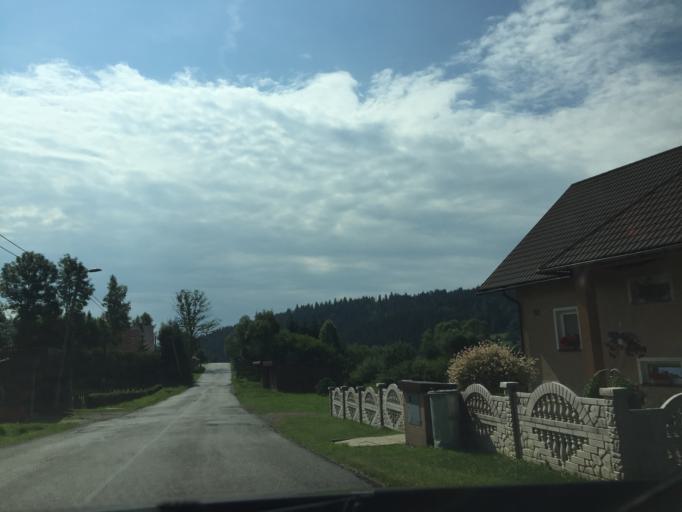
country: PL
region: Silesian Voivodeship
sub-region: Powiat zywiecki
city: Sopotnia Wielka
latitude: 49.4382
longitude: 19.3152
